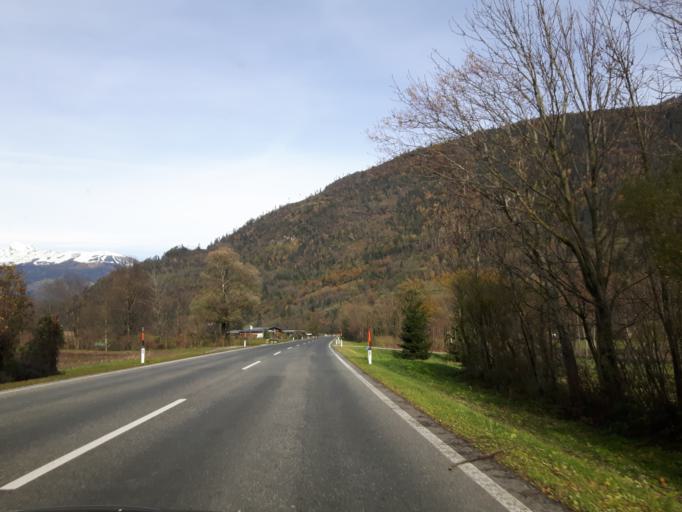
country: AT
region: Tyrol
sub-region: Politischer Bezirk Lienz
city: Lavant
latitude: 46.7927
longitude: 12.8754
